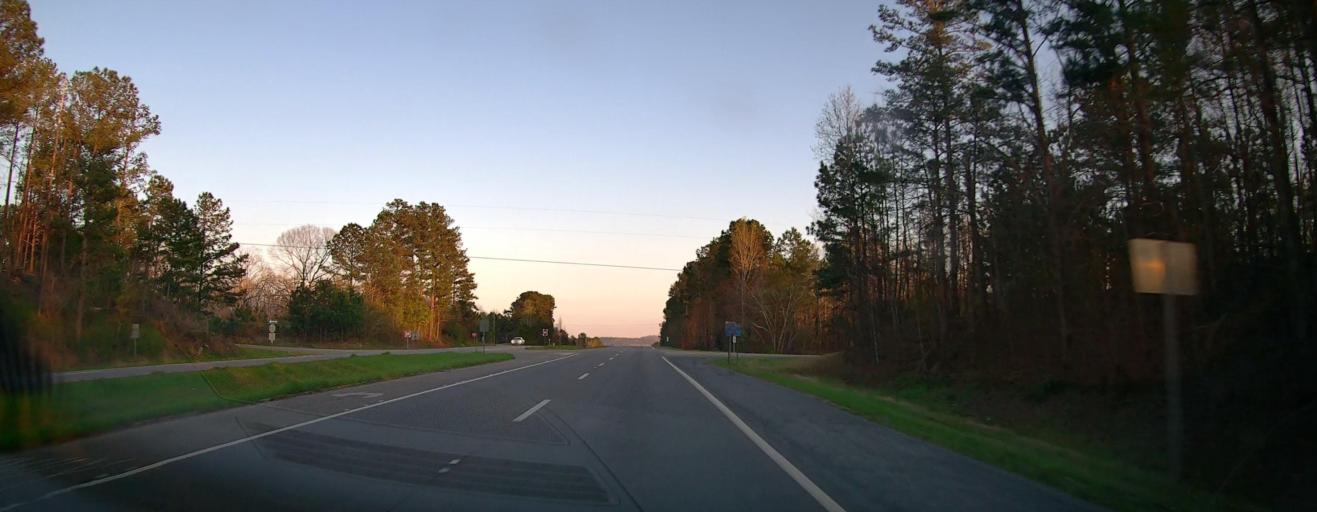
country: US
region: Alabama
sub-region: Coosa County
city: Stewartville
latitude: 33.1084
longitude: -86.2313
